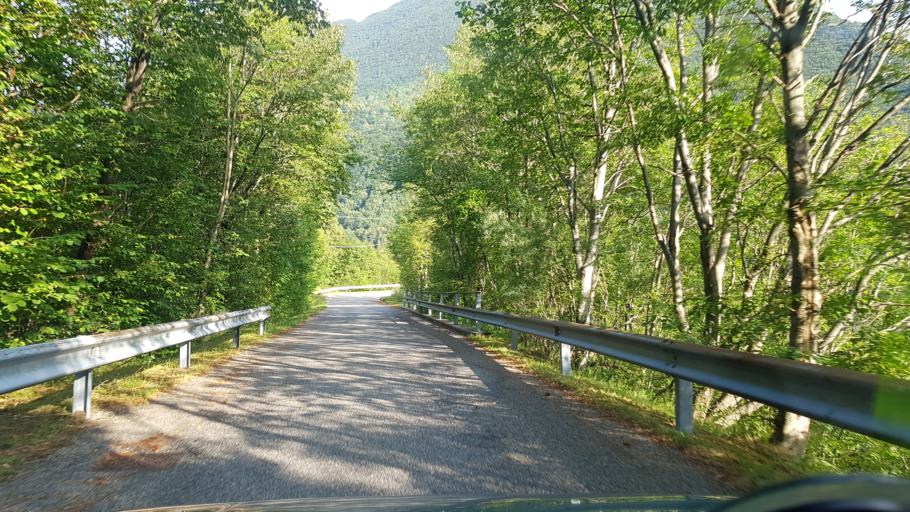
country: IT
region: Friuli Venezia Giulia
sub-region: Provincia di Udine
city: Lusevera
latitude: 46.3115
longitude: 13.2734
